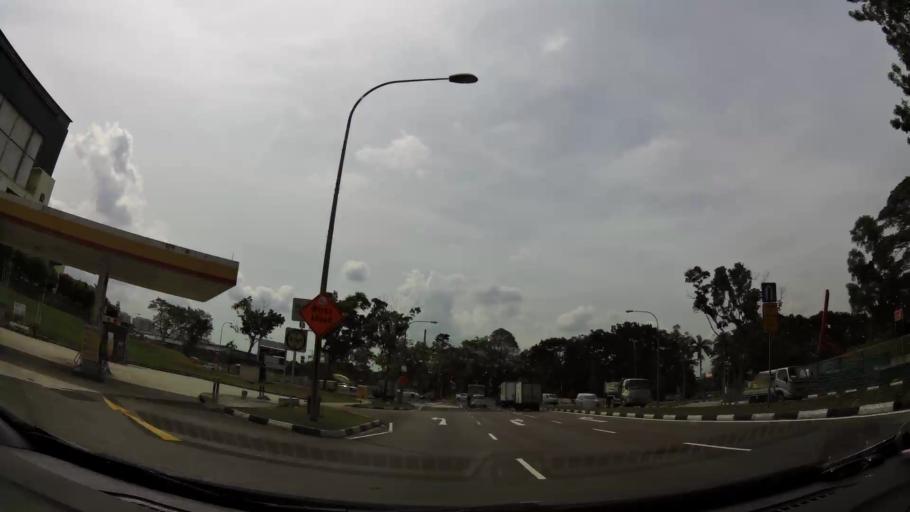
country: MY
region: Johor
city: Johor Bahru
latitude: 1.4117
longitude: 103.7566
